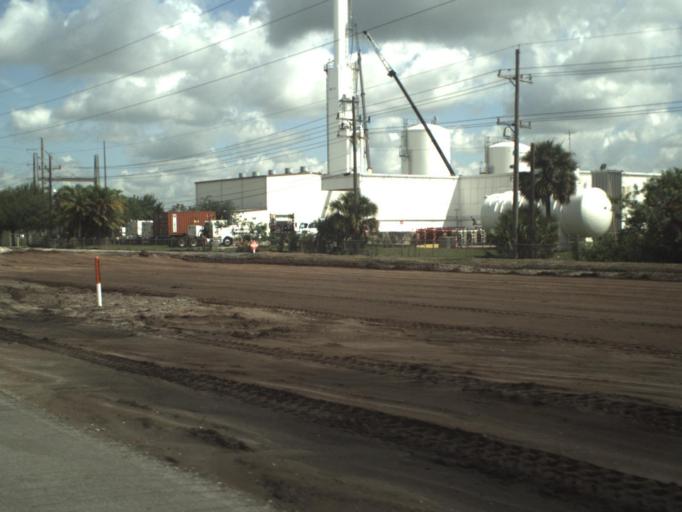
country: US
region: Florida
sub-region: Palm Beach County
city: Limestone Creek
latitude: 26.9181
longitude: -80.3145
